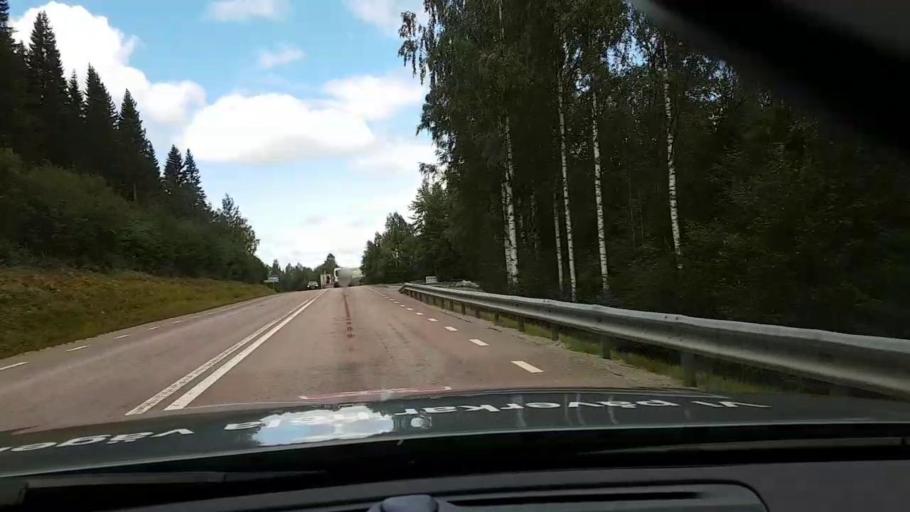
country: SE
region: Vaesternorrland
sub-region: OErnskoeldsviks Kommun
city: Bjasta
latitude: 63.3611
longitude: 18.4638
